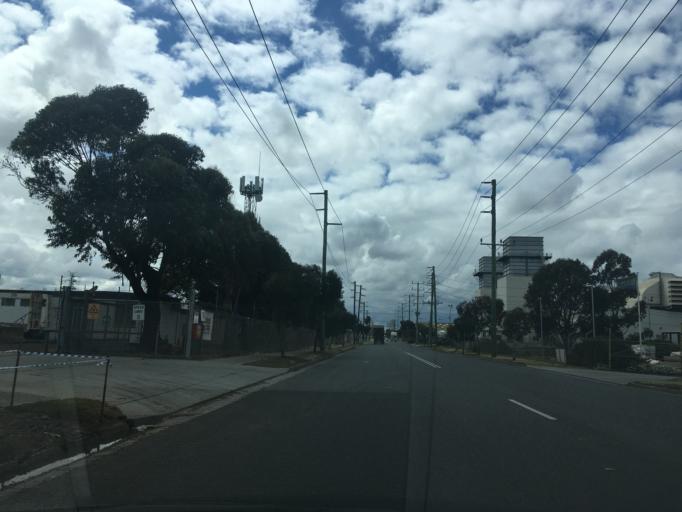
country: AU
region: Victoria
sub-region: Hobsons Bay
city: Laverton
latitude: -37.8419
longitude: 144.7864
